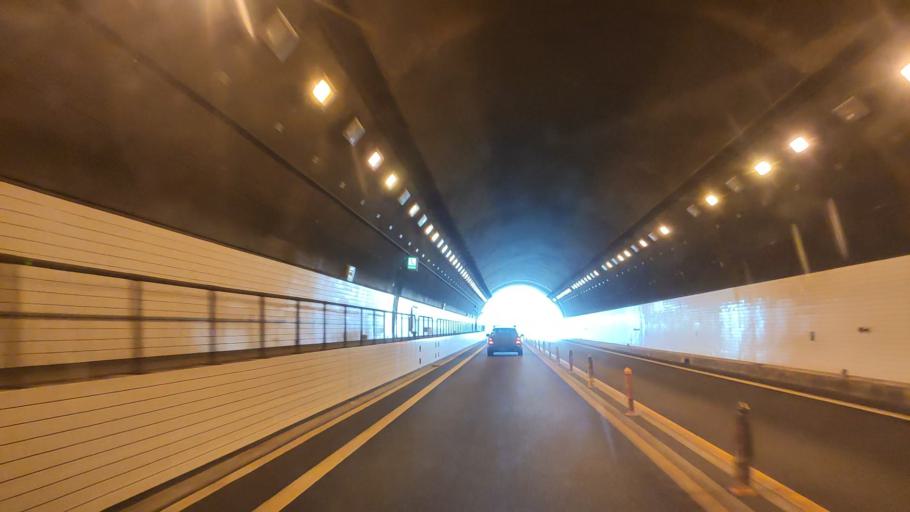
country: JP
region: Tokushima
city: Ikedacho
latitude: 34.0166
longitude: 133.7544
